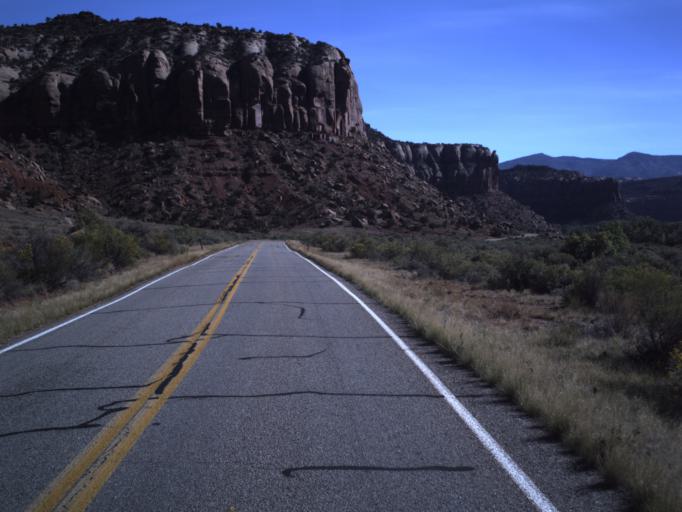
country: US
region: Utah
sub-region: San Juan County
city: Monticello
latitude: 38.0539
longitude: -109.5534
